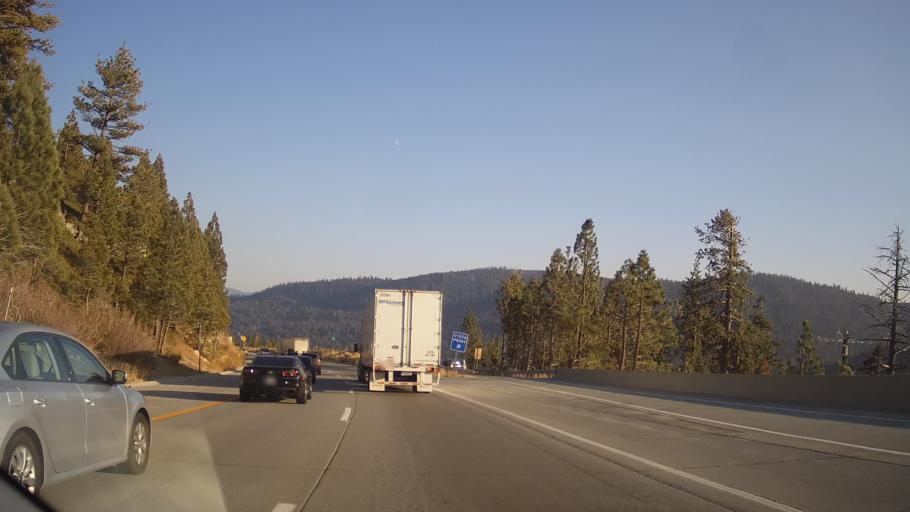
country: US
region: California
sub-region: Nevada County
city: Truckee
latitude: 39.3278
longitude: -120.3007
